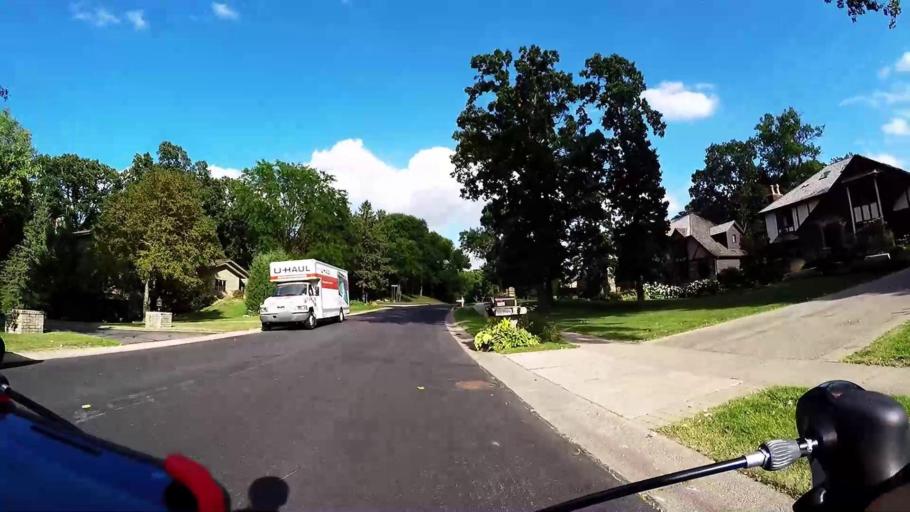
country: US
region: Minnesota
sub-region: Hennepin County
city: Eden Prairie
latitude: 44.8799
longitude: -93.4456
